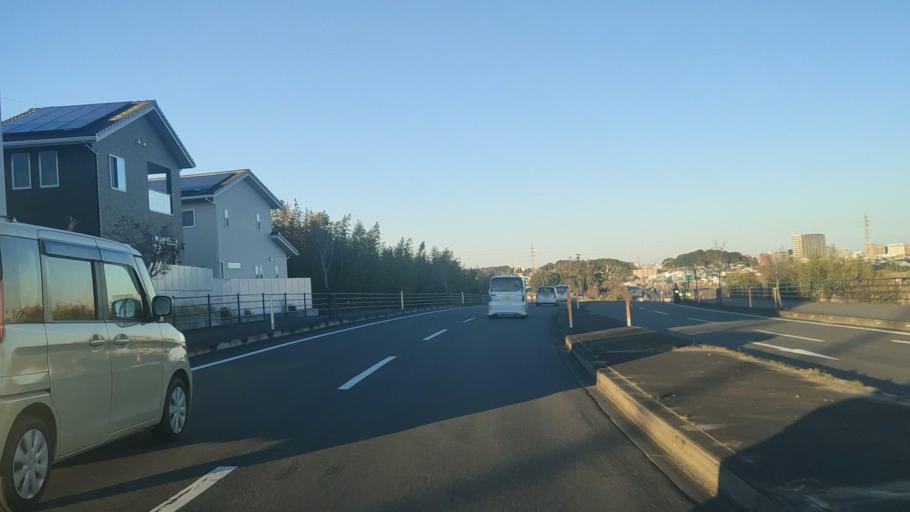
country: JP
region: Miyazaki
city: Miyazaki-shi
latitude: 31.8900
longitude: 131.4033
